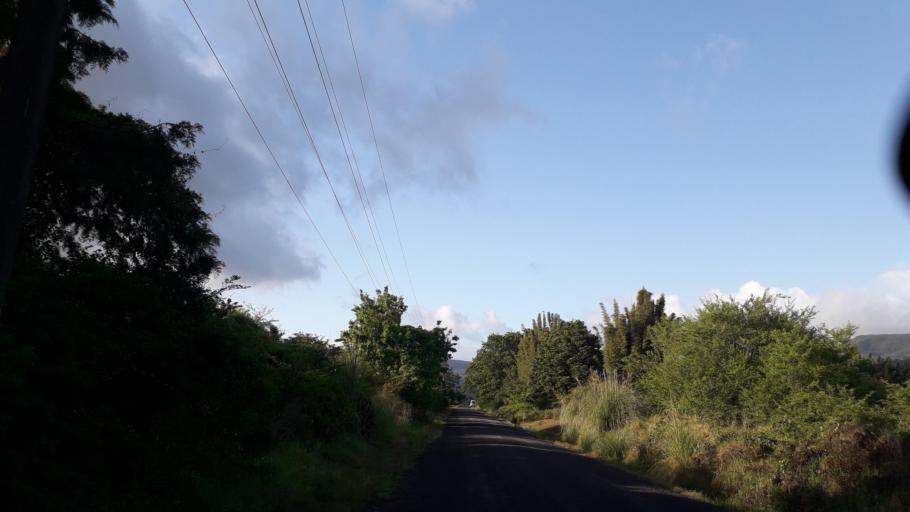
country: NZ
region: Northland
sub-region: Far North District
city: Waimate North
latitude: -35.4958
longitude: 173.6994
